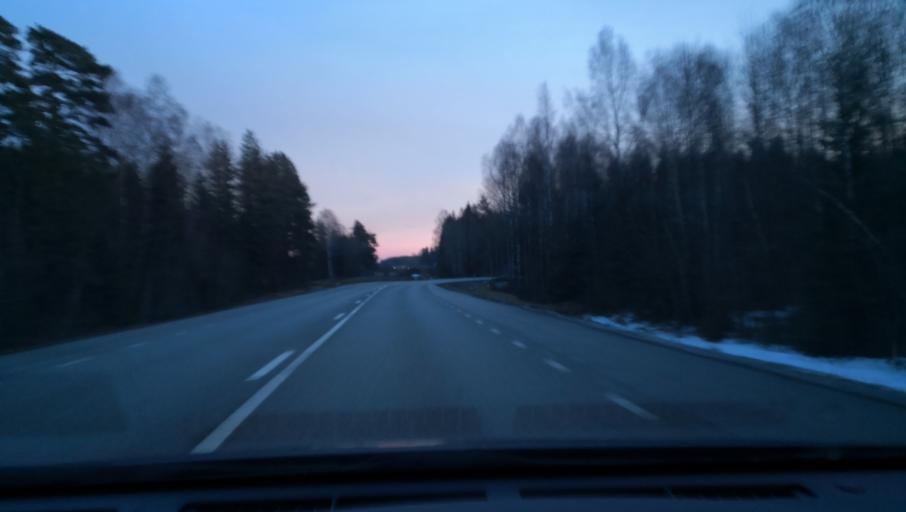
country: SE
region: OErebro
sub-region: Orebro Kommun
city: Orebro
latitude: 59.2411
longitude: 15.0986
